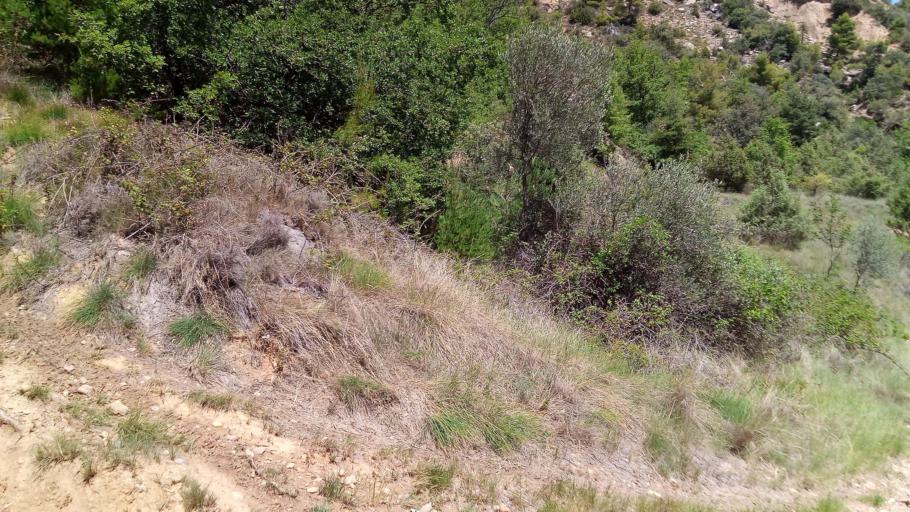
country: ES
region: Aragon
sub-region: Provincia de Huesca
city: Lascuarre
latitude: 42.2670
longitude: 0.4896
